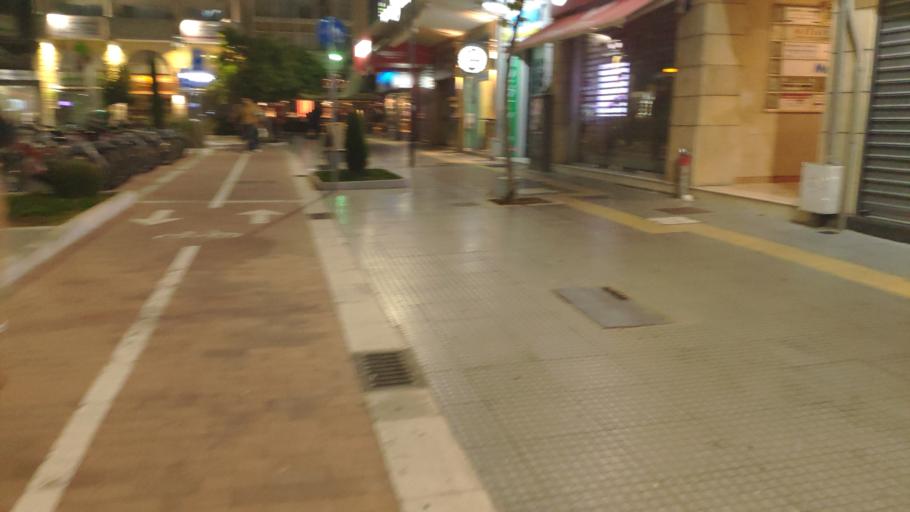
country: GR
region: Thessaly
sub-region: Nomos Larisis
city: Larisa
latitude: 39.6384
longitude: 22.4167
